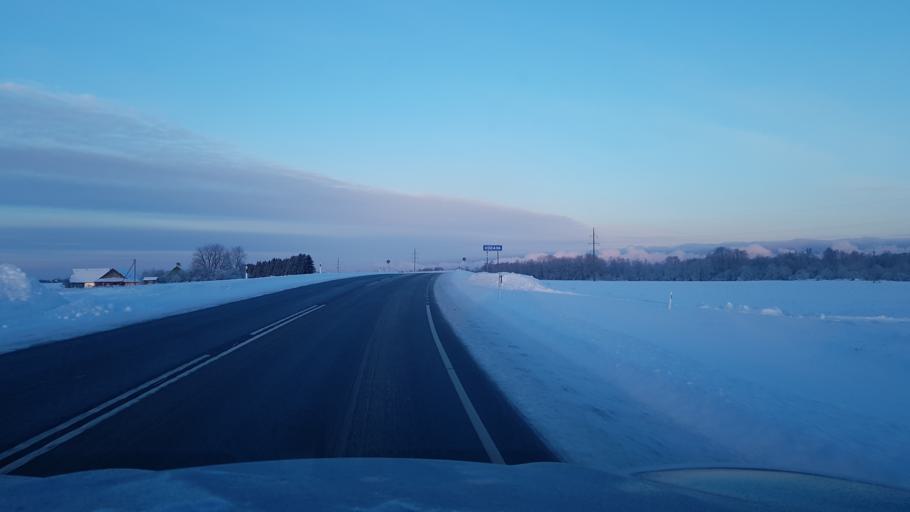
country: EE
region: Ida-Virumaa
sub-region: Narva-Joesuu linn
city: Narva-Joesuu
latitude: 59.4030
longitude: 28.0539
